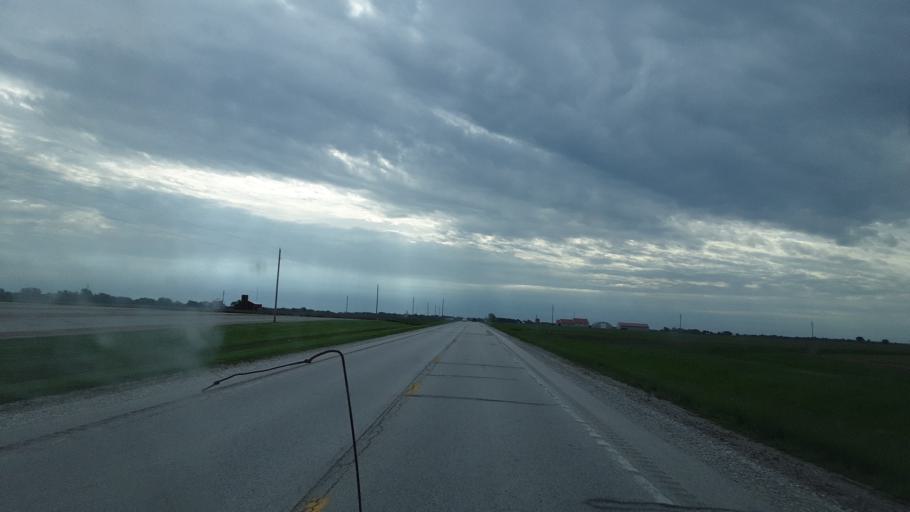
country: US
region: Illinois
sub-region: Hancock County
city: Hamilton
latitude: 40.3958
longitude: -91.2982
